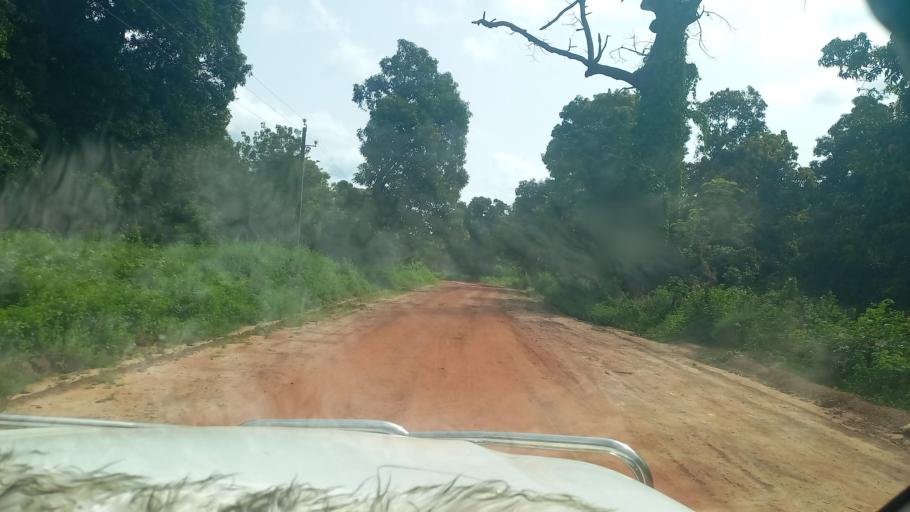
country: SN
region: Ziguinchor
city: Bignona
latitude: 12.7522
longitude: -16.2775
